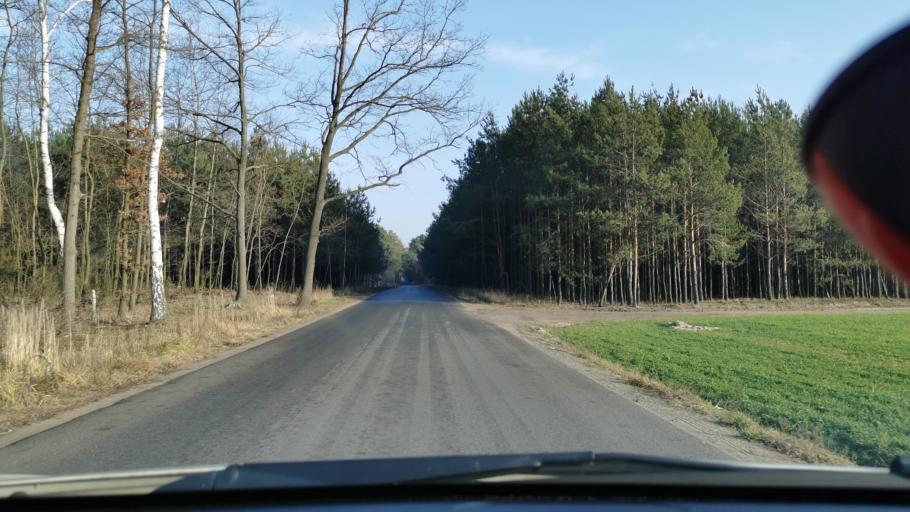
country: PL
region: Greater Poland Voivodeship
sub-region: Powiat kaliski
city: Opatowek
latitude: 51.6602
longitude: 18.2591
